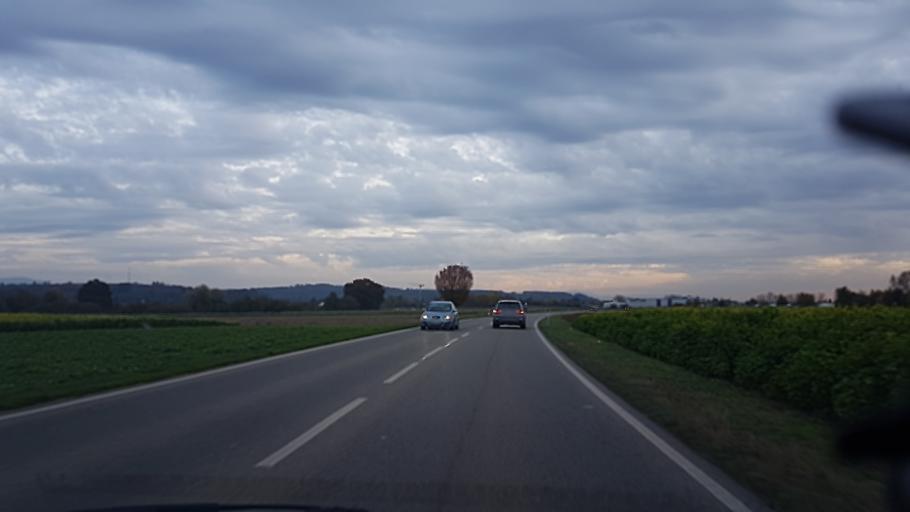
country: DE
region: Baden-Wuerttemberg
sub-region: Freiburg Region
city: Kenzingen
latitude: 48.2104
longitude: 7.7610
